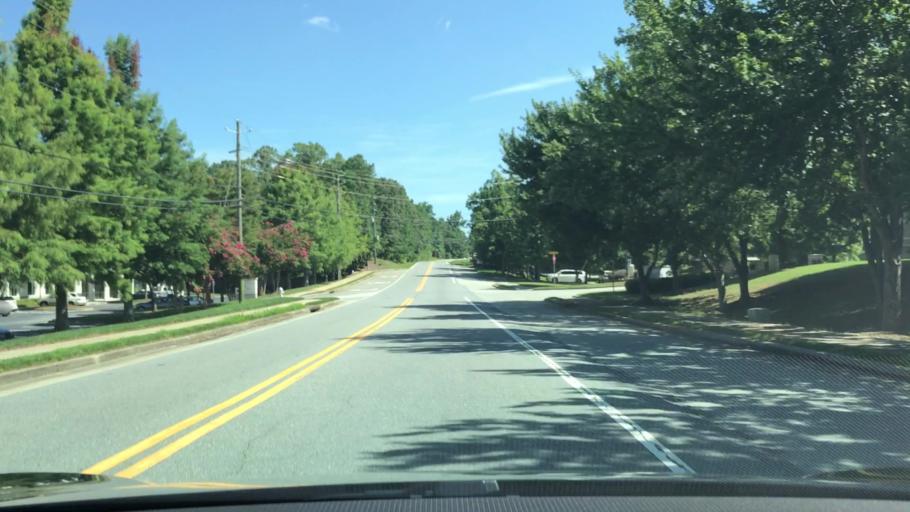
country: US
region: Georgia
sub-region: Gwinnett County
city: Suwanee
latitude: 34.0643
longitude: -84.0637
